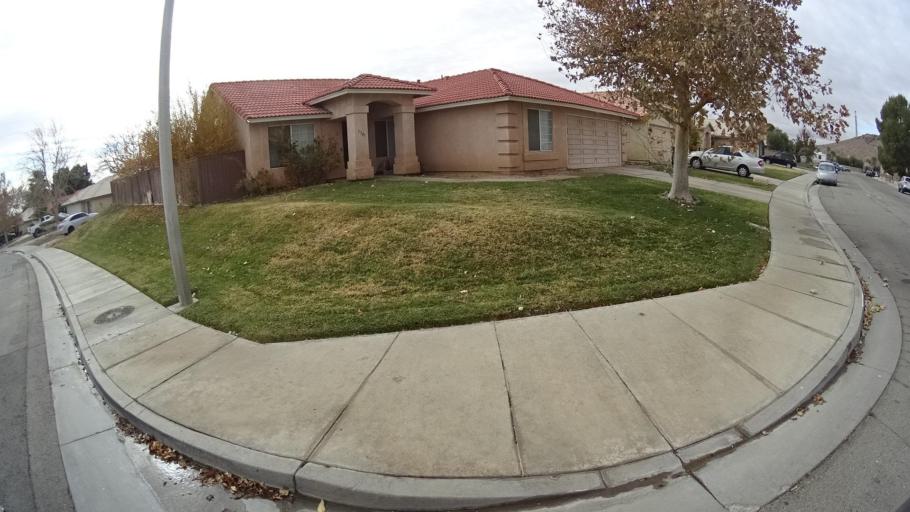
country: US
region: California
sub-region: Kern County
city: Rosamond
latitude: 34.8756
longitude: -118.1545
